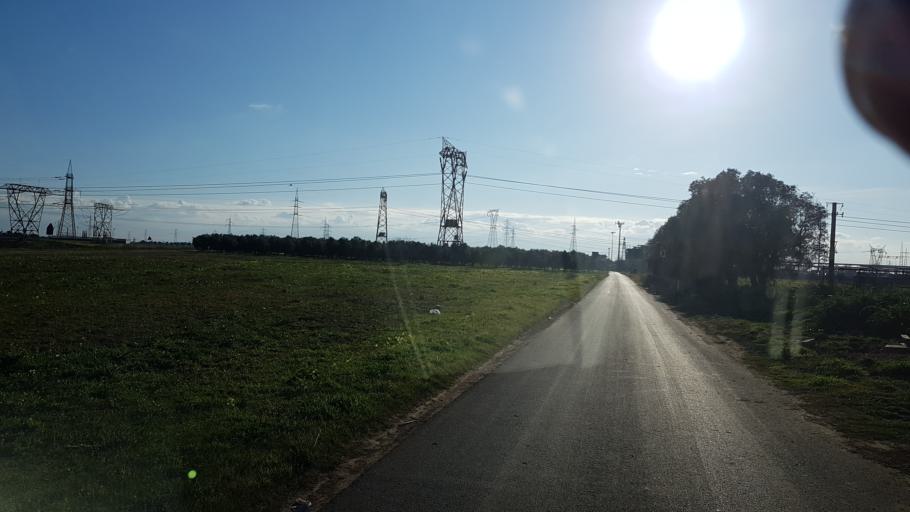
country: IT
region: Apulia
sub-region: Provincia di Brindisi
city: Brindisi
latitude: 40.6034
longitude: 17.9071
